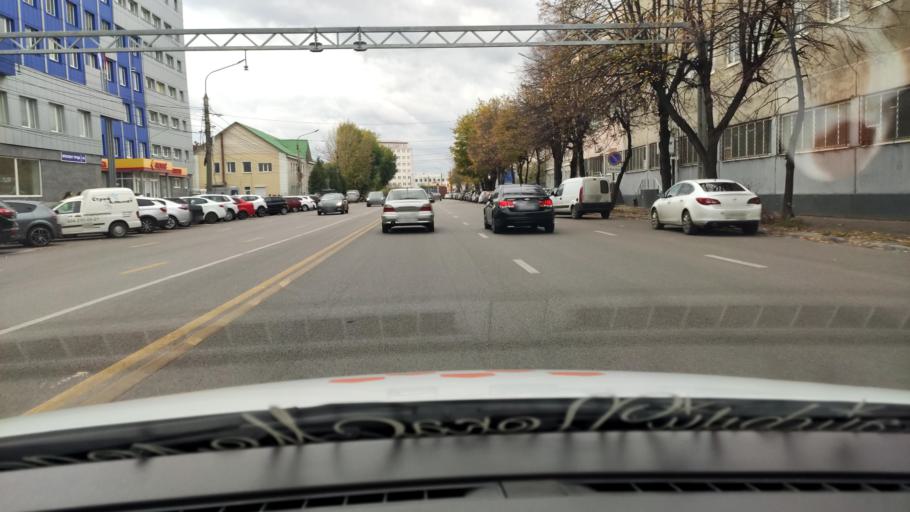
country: RU
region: Voronezj
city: Voronezh
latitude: 51.6806
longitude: 39.1816
